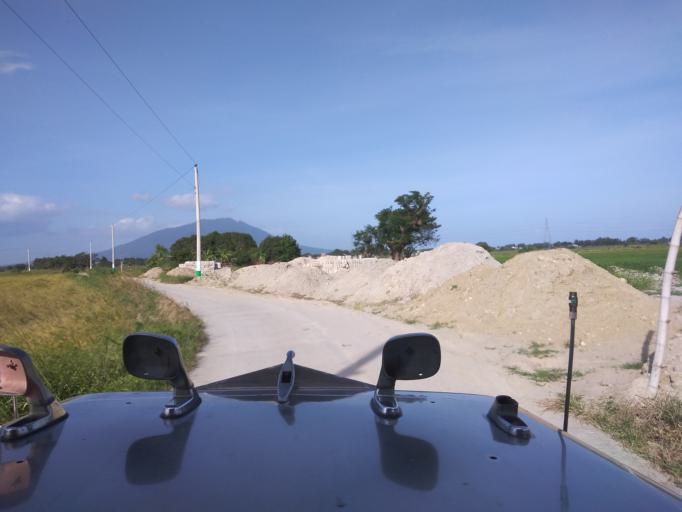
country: PH
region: Central Luzon
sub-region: Province of Pampanga
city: San Patricio
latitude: 15.0984
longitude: 120.6943
